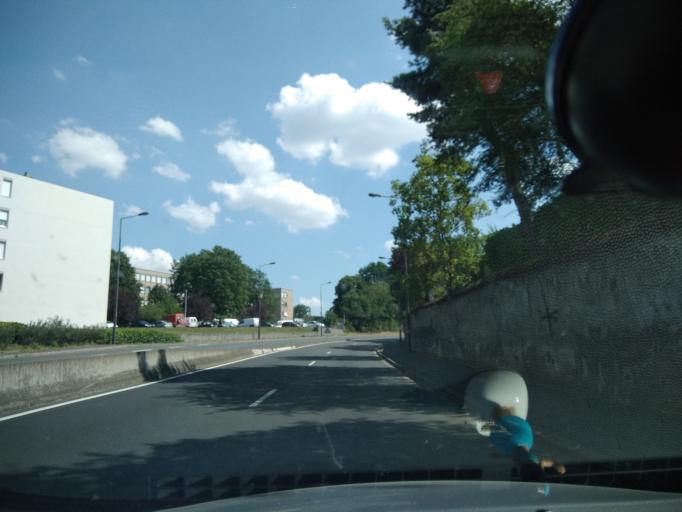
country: FR
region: Centre
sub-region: Departement d'Indre-et-Loire
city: Tours
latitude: 47.3616
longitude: 0.6962
